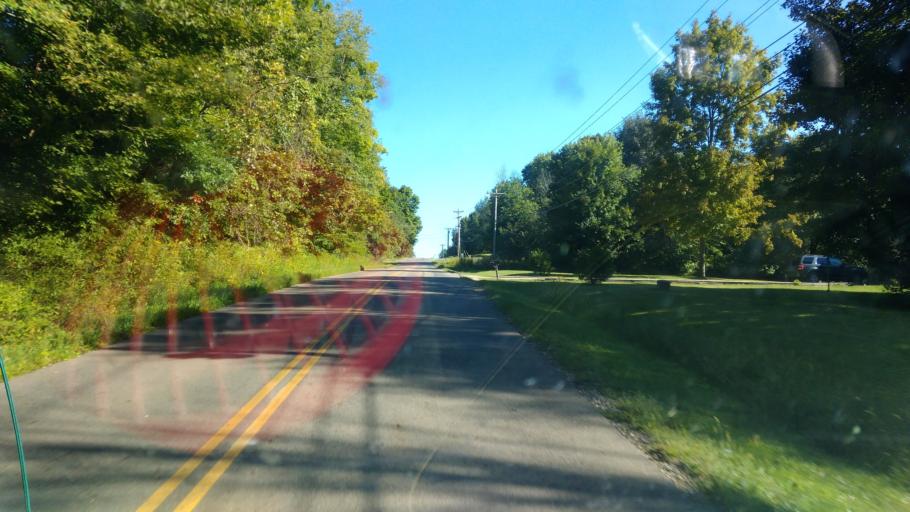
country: US
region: Ohio
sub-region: Knox County
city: Gambier
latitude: 40.4419
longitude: -82.3667
